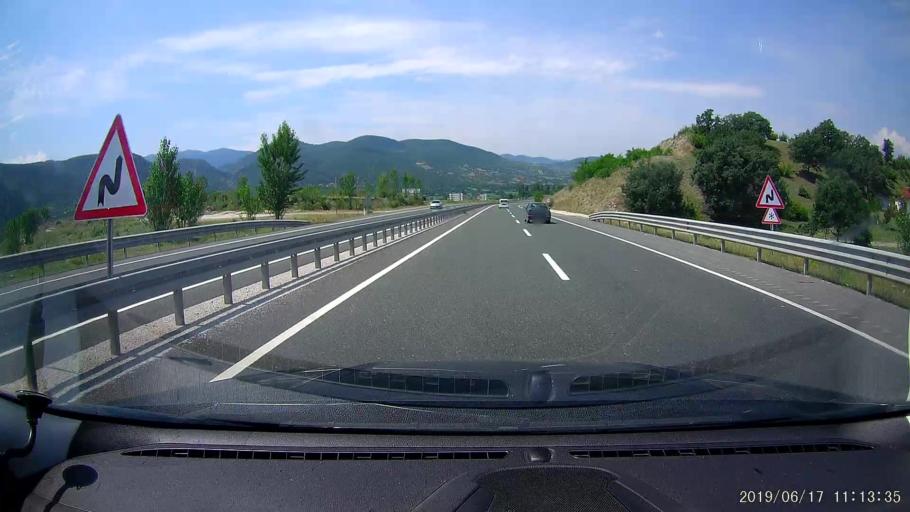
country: TR
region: Kastamonu
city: Tosya
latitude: 40.9599
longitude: 33.9692
